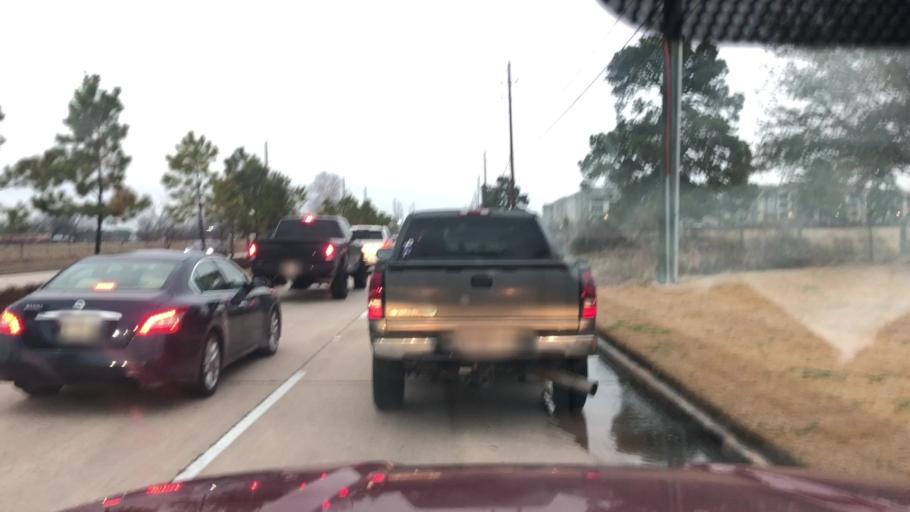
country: US
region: Texas
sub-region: Harris County
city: Tomball
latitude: 30.0415
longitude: -95.5377
